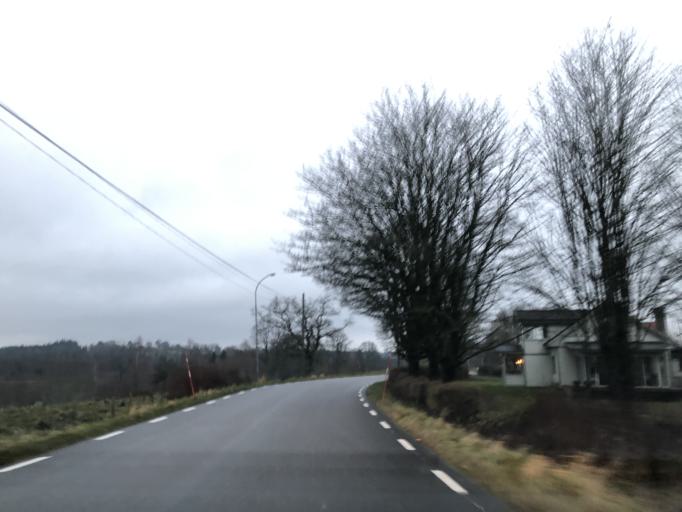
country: SE
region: Vaestra Goetaland
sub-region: Boras Kommun
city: Dalsjofors
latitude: 57.8390
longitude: 13.2243
